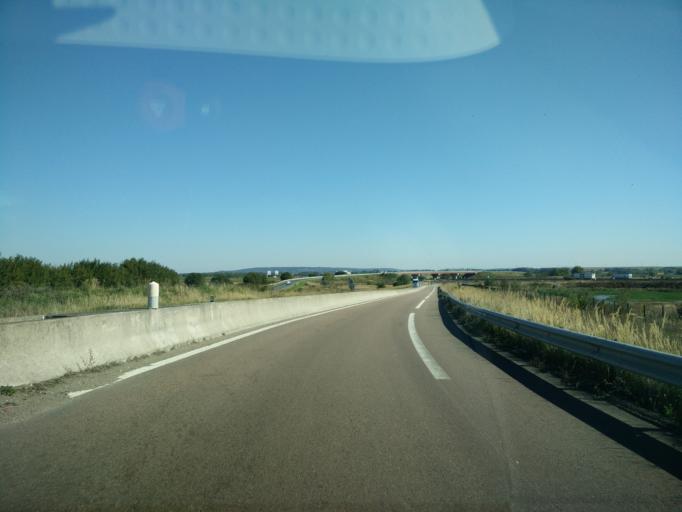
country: FR
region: Ile-de-France
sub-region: Departement de Seine-et-Marne
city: Mitry-Mory
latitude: 49.0024
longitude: 2.6345
